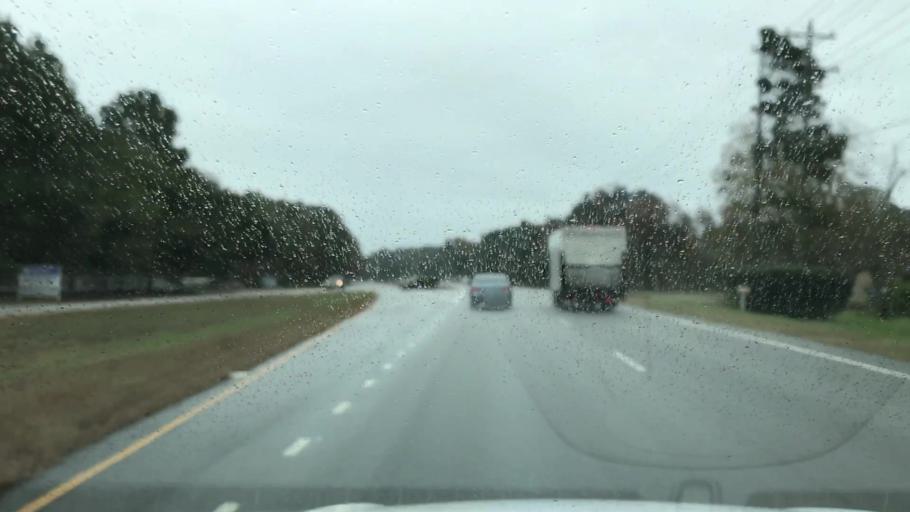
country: US
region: South Carolina
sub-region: Charleston County
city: Isle of Palms
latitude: 32.8869
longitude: -79.7448
